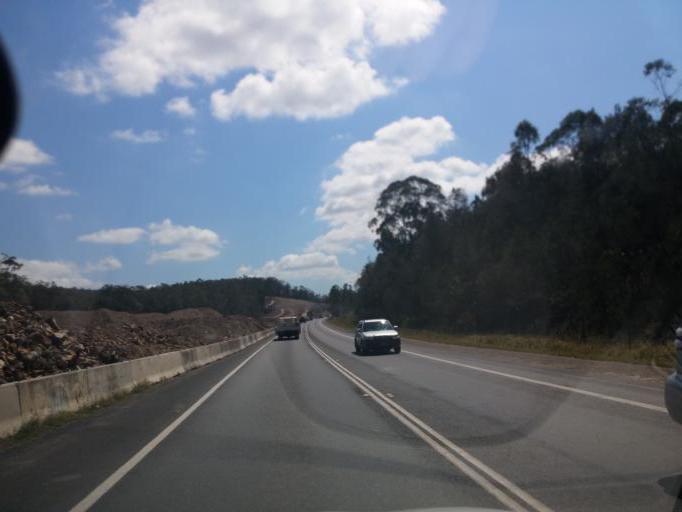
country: AU
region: New South Wales
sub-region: Port Macquarie-Hastings
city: North Shore
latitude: -31.2742
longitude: 152.8125
